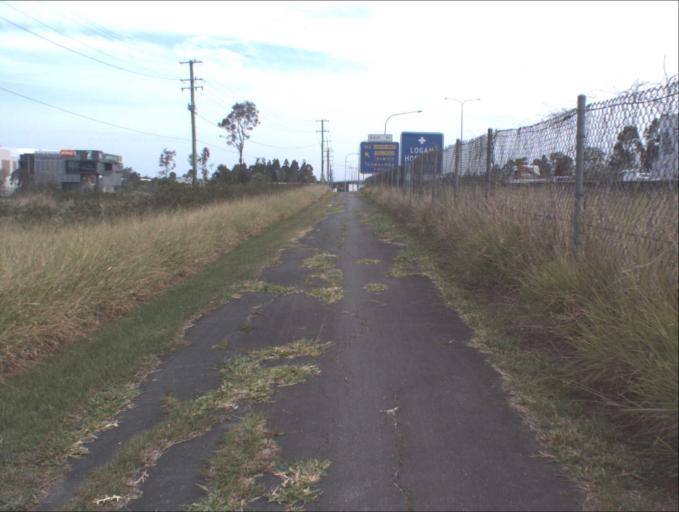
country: AU
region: Queensland
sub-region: Logan
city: Beenleigh
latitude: -27.6804
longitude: 153.1871
